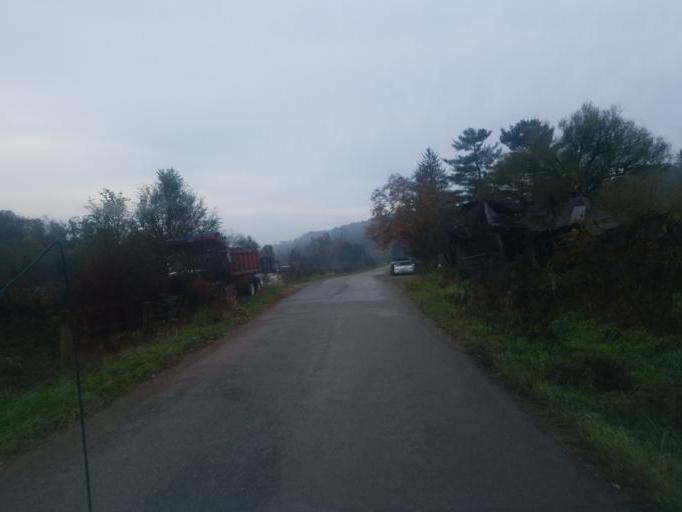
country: US
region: Ohio
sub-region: Athens County
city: Glouster
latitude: 39.5105
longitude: -81.9495
